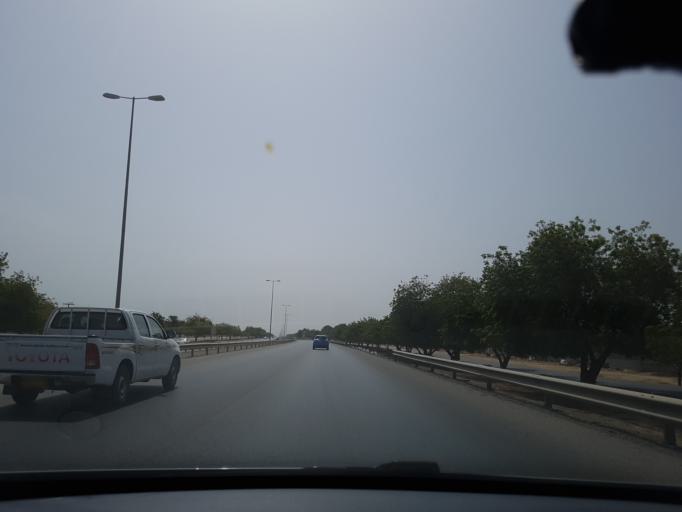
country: OM
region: Al Batinah
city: As Suwayq
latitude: 23.8432
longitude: 57.3667
